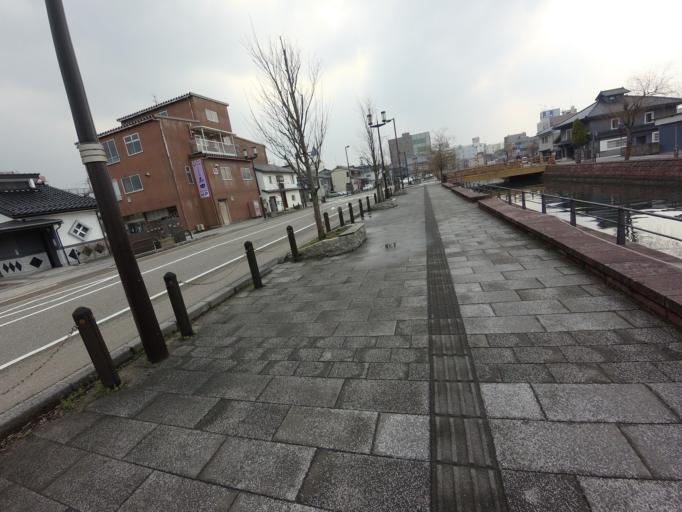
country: JP
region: Ishikawa
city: Nanao
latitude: 37.0466
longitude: 136.9663
